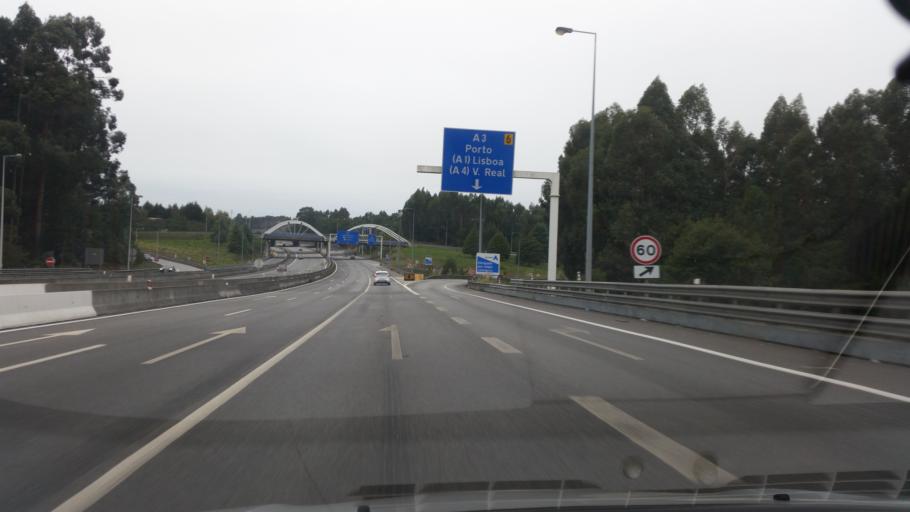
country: PT
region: Porto
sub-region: Valongo
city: Ermesinde
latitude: 41.2407
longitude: -8.5578
